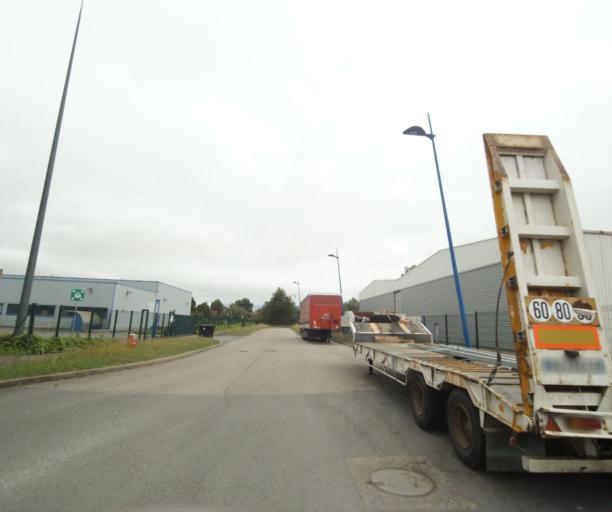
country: FR
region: Rhone-Alpes
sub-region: Departement de l'Ain
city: Mionnay
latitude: 45.8721
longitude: 4.9202
